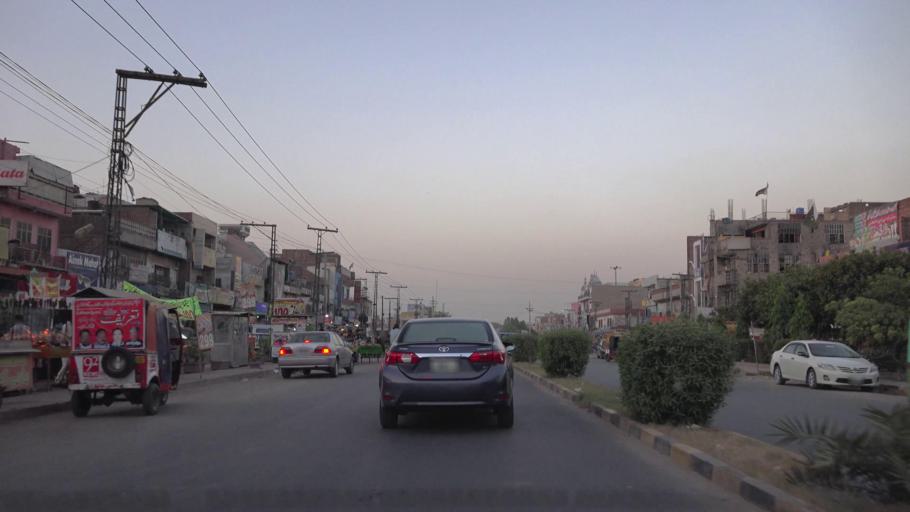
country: PK
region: Punjab
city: Faisalabad
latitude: 31.4503
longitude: 73.0979
